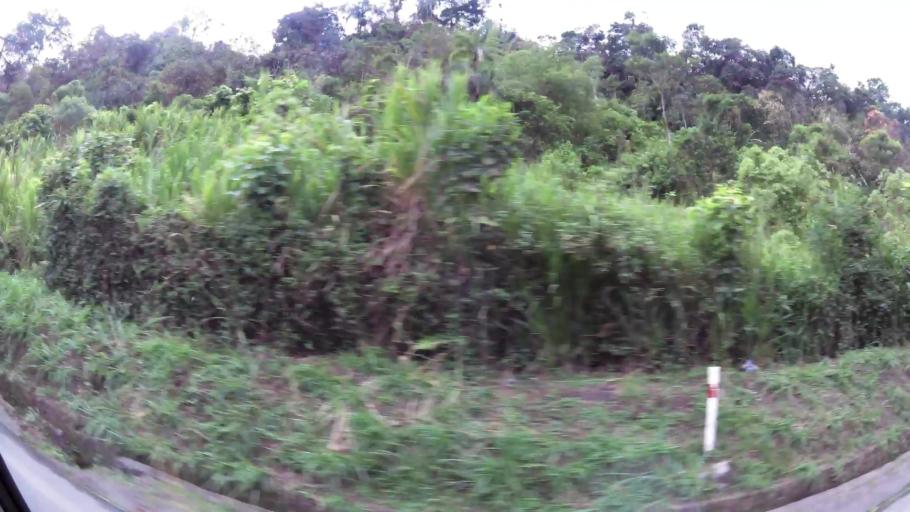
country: EC
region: Santo Domingo de los Tsachilas
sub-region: Canton Santo Domingo de los Colorados
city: Santo Domingo de los Colorados
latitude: -0.3173
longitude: -79.0112
